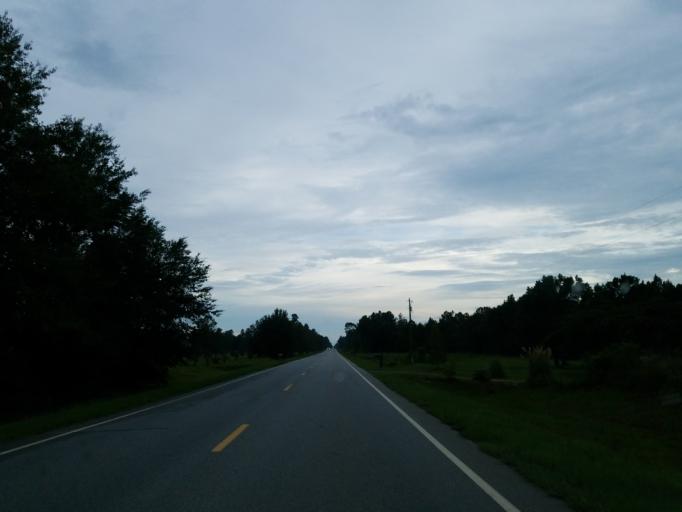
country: US
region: Georgia
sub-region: Lanier County
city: Lakeland
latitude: 30.9682
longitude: -83.0066
